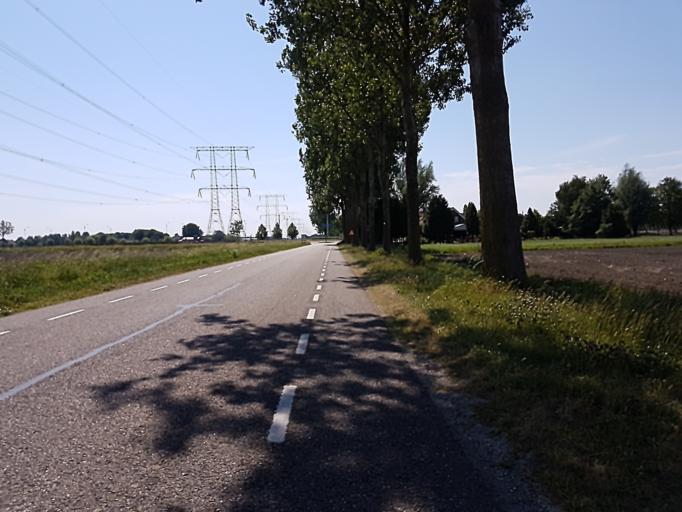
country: NL
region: North Brabant
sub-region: Gemeente Dongen
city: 's Gravenmoer
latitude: 51.6504
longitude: 4.9889
